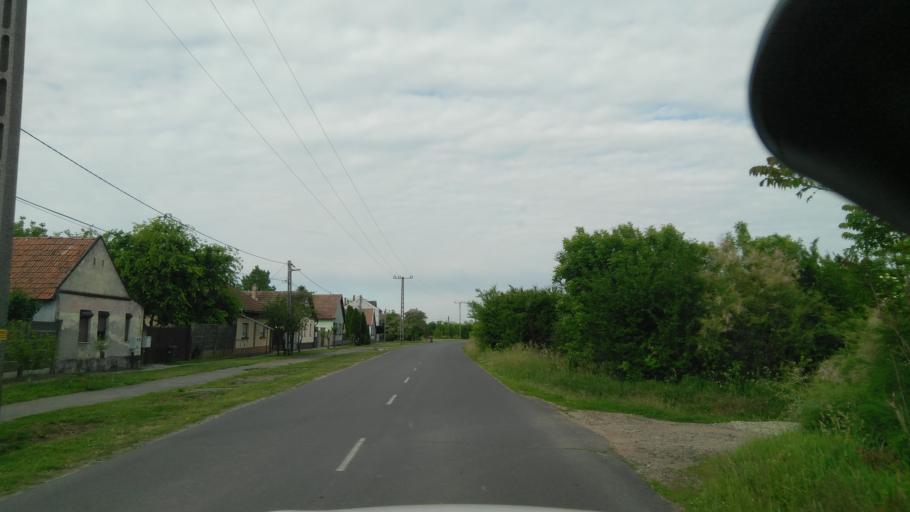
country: HU
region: Bekes
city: Ketegyhaza
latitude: 46.5411
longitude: 21.1712
